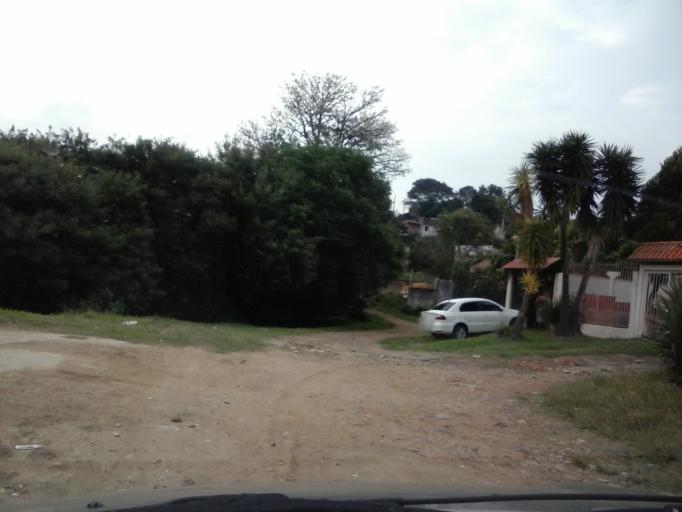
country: BR
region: Rio Grande do Sul
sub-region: Porto Alegre
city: Porto Alegre
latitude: -30.0544
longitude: -51.1535
